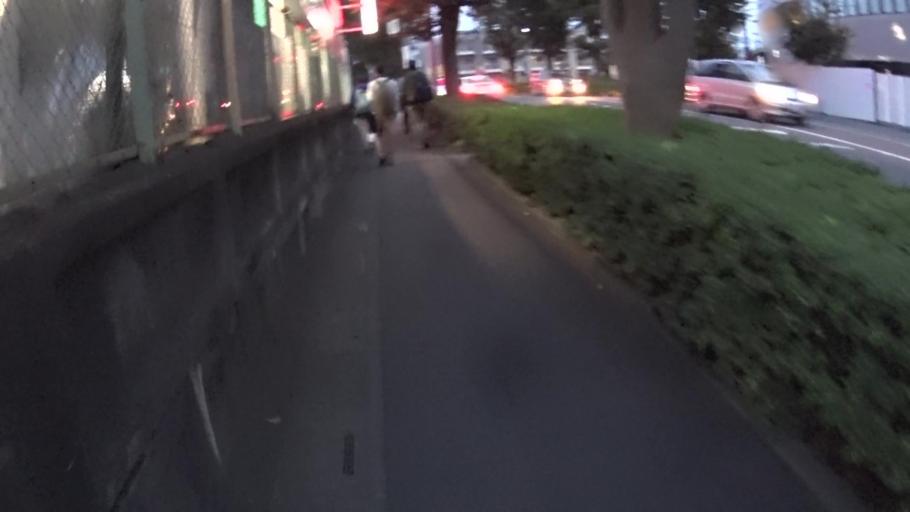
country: JP
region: Saitama
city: Hanno
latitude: 35.8491
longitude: 139.3175
